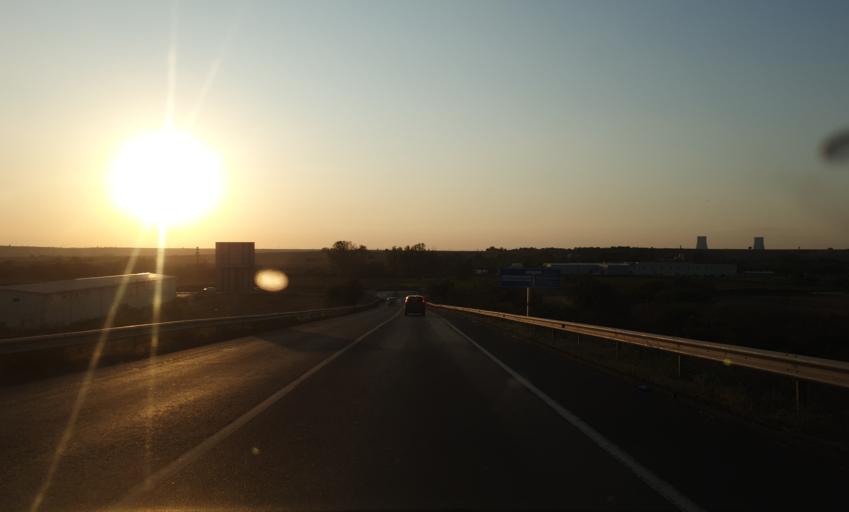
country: TR
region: Kirklareli
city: Luleburgaz
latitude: 41.4418
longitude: 27.3824
